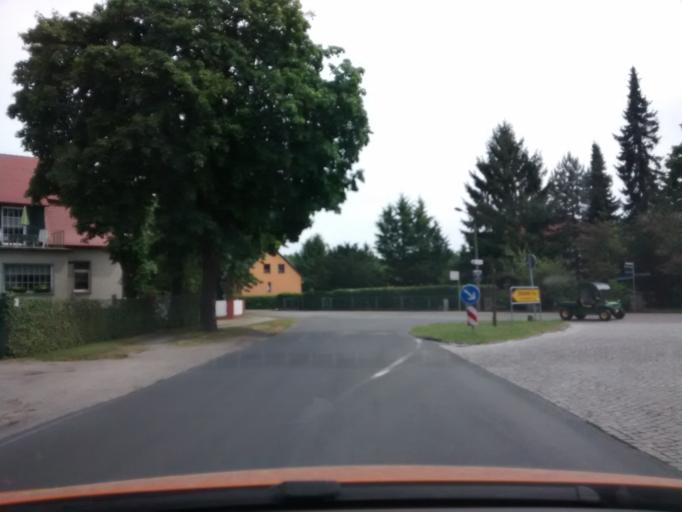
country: DE
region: Saxony-Anhalt
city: Holzdorf
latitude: 51.8149
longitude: 13.2187
